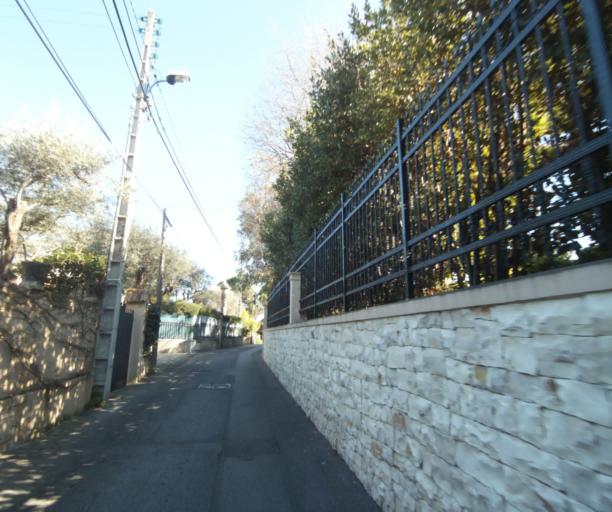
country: FR
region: Provence-Alpes-Cote d'Azur
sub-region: Departement des Alpes-Maritimes
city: Antibes
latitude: 43.5673
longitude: 7.1216
